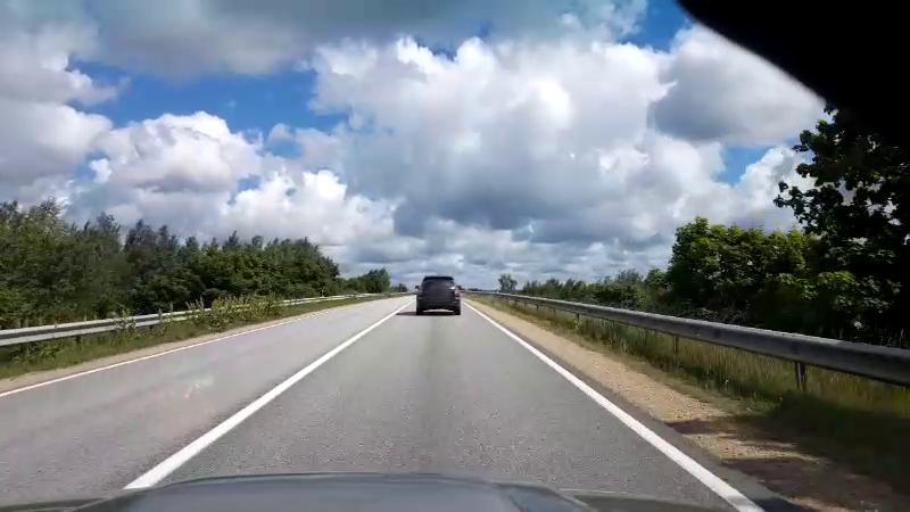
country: LV
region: Salaspils
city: Salaspils
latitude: 56.8530
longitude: 24.4005
